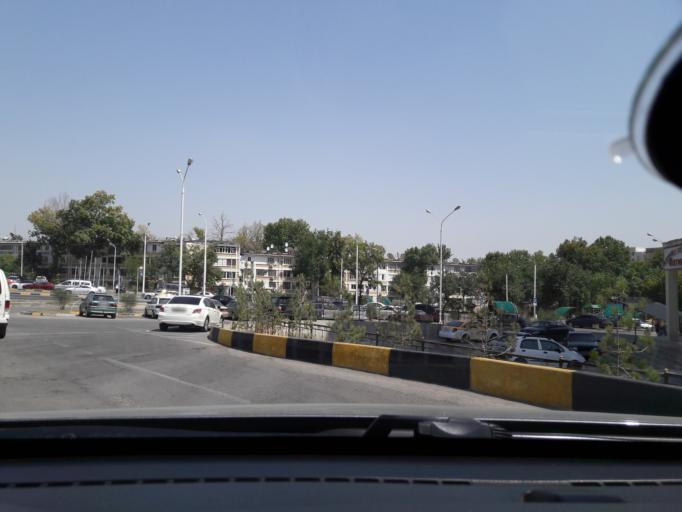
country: TJ
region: Dushanbe
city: Dushanbe
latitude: 38.5900
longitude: 68.7321
